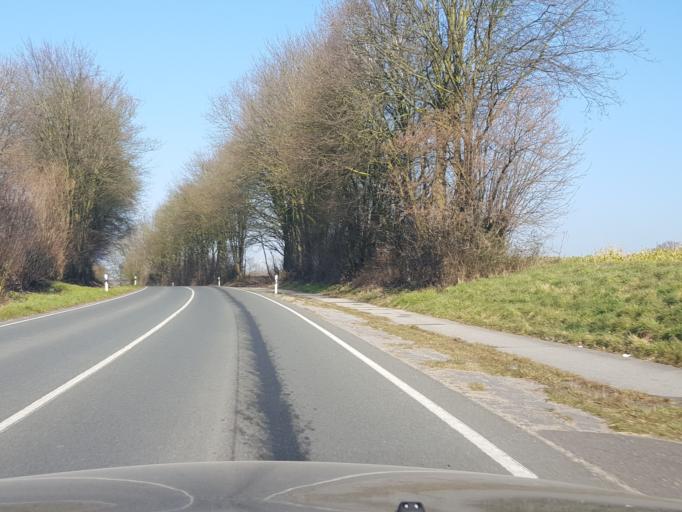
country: DE
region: North Rhine-Westphalia
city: Oer-Erkenschwick
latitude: 51.6508
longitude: 7.2298
